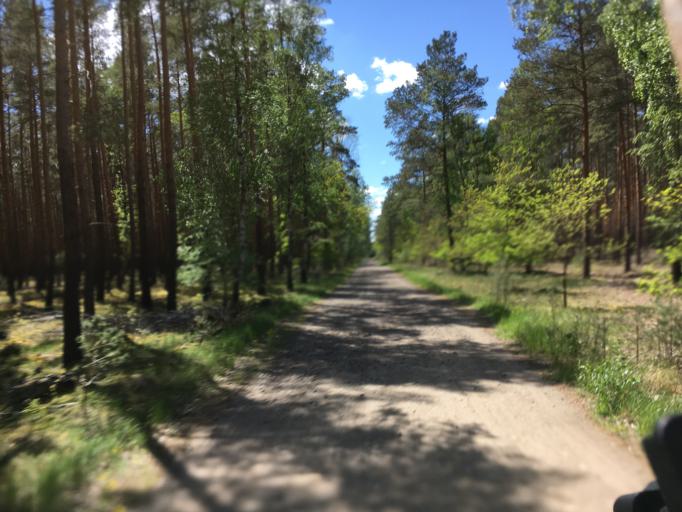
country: DE
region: Brandenburg
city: Trebbin
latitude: 52.1633
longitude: 13.2076
